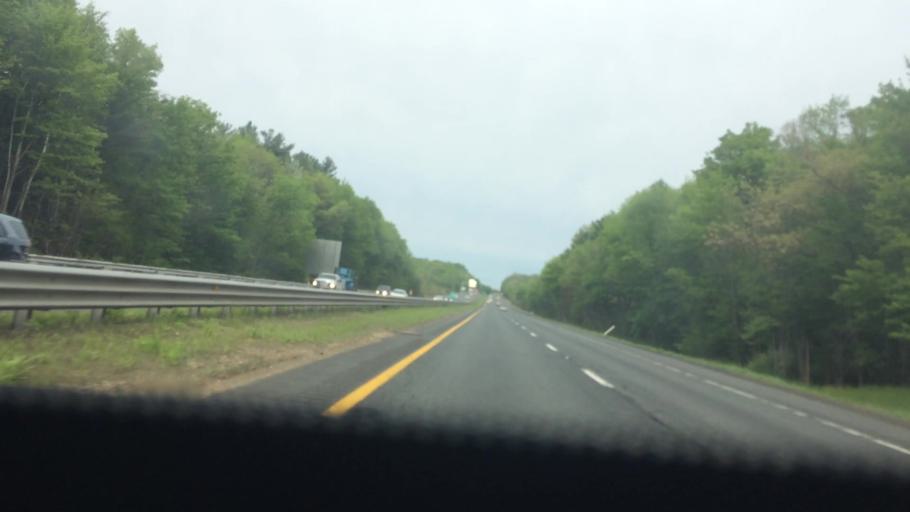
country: US
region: Massachusetts
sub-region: Worcester County
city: Fiskdale
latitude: 42.1353
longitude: -72.0963
